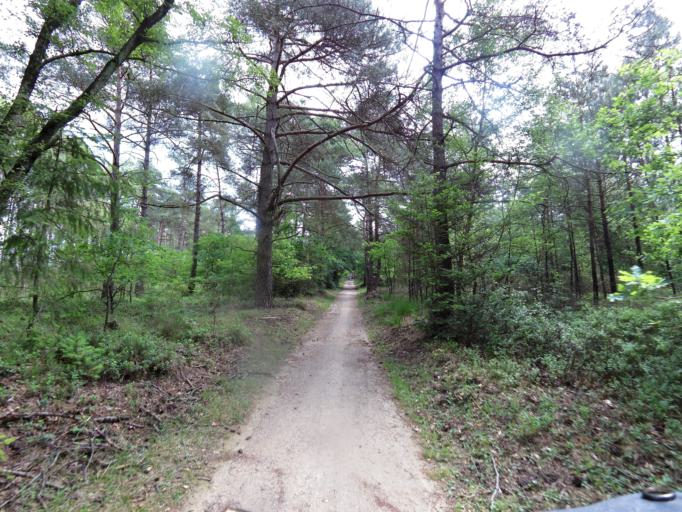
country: NL
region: Gelderland
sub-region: Gemeente Apeldoorn
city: Uddel
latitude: 52.2994
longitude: 5.8262
